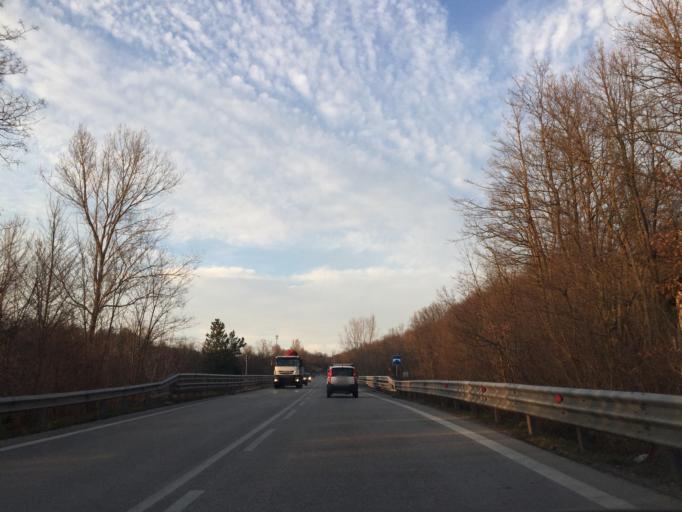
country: IT
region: Molise
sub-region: Provincia di Campobasso
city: Vinchiaturo
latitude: 41.5085
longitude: 14.6078
